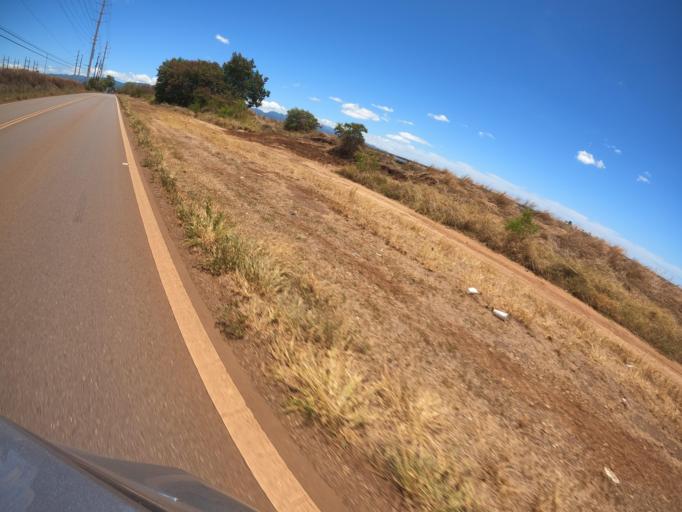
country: US
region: Hawaii
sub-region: Honolulu County
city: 'Ewa Villages
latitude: 21.3700
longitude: -158.0474
